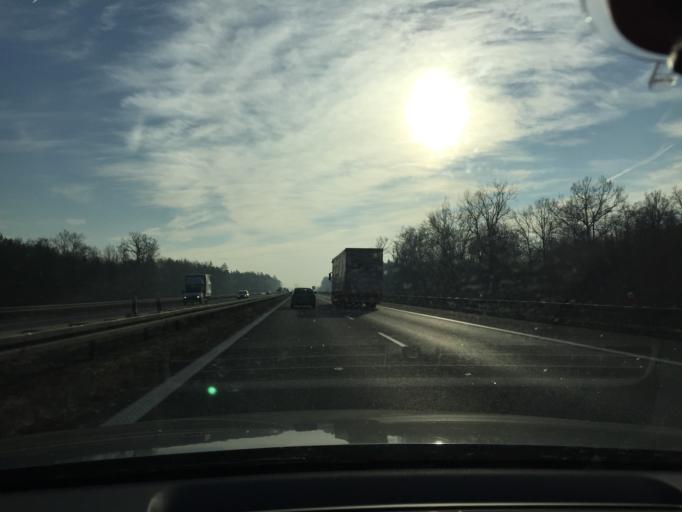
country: PL
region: Silesian Voivodeship
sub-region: Powiat gliwicki
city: Sosnicowice
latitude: 50.3253
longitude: 18.5474
